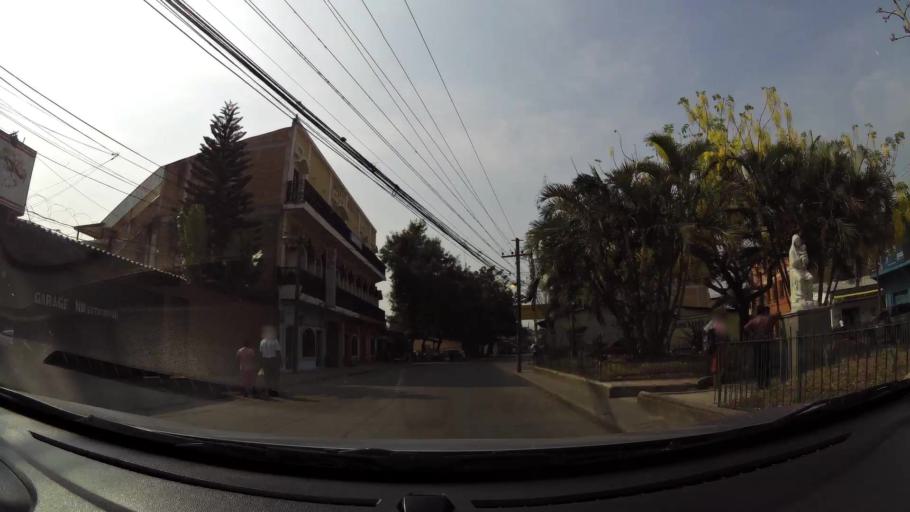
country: HN
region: Comayagua
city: Comayagua
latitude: 14.4557
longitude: -87.6396
